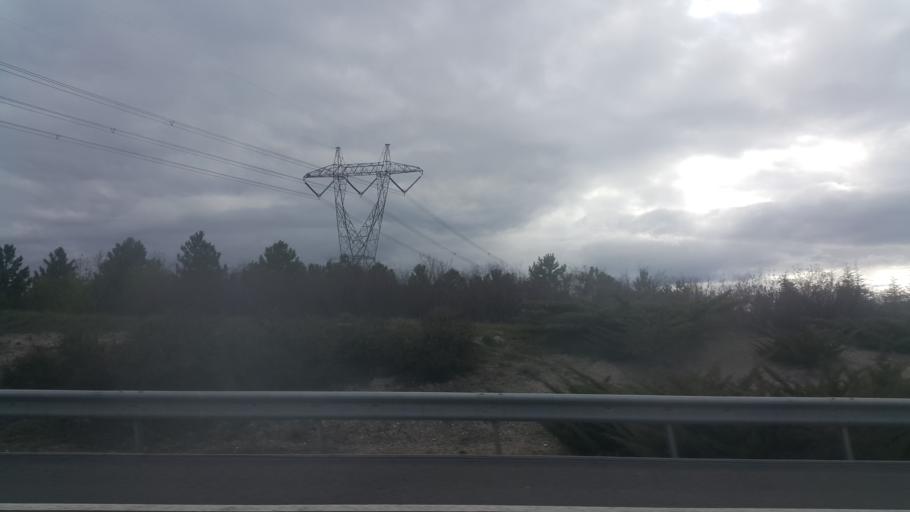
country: TR
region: Ankara
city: Etimesgut
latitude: 40.0087
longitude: 32.6310
